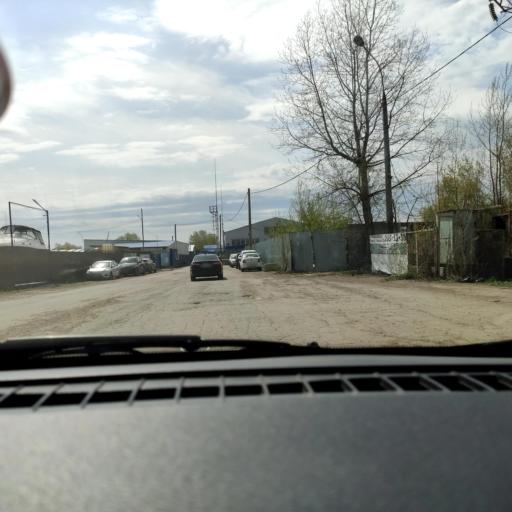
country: RU
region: Samara
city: Samara
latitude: 53.1764
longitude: 50.1236
